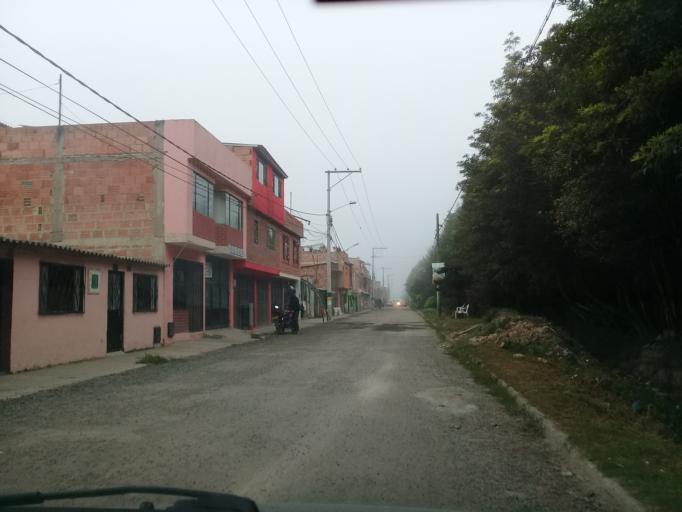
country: CO
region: Cundinamarca
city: Madrid
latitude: 4.7255
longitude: -74.2469
